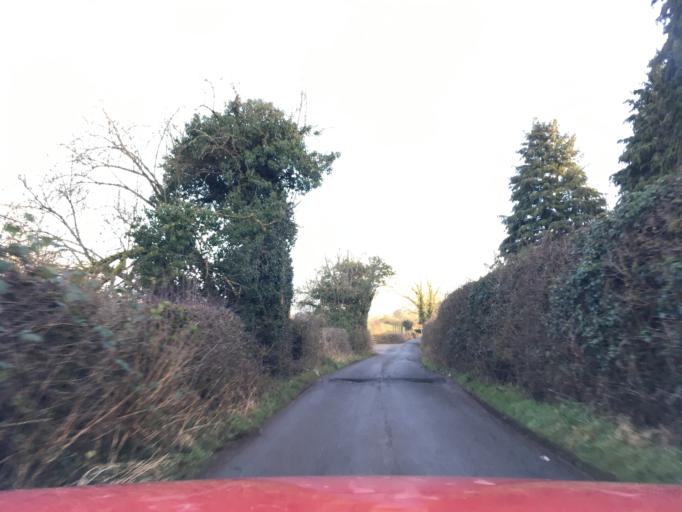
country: GB
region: England
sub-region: Warwickshire
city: Stratford-upon-Avon
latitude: 52.2089
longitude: -1.6910
